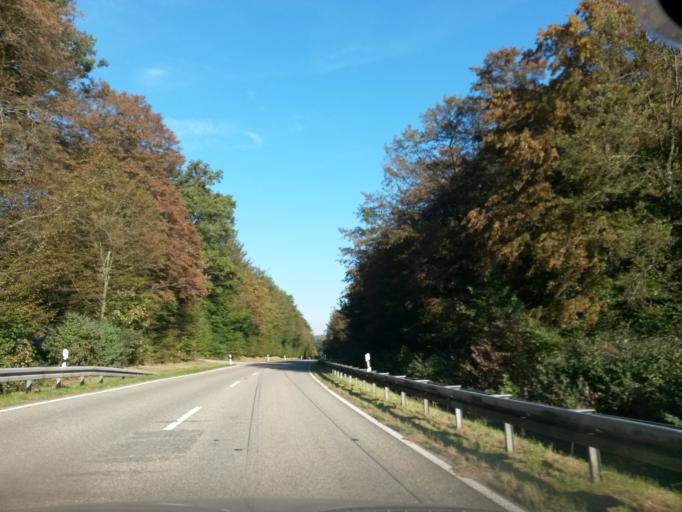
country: DE
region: Baden-Wuerttemberg
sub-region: Karlsruhe Region
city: Konigsbach-Stein
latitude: 48.9336
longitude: 8.5109
